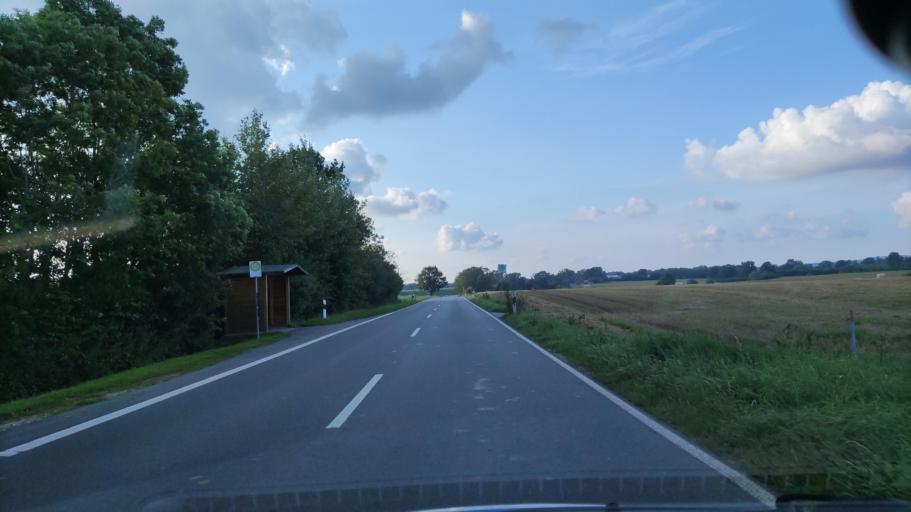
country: DE
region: Schleswig-Holstein
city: Glasau
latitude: 54.0400
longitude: 10.5381
